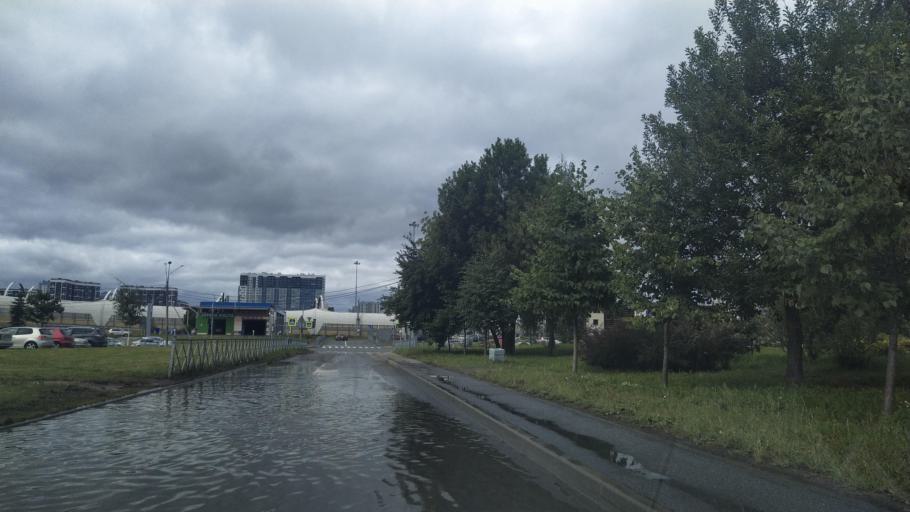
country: RU
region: St.-Petersburg
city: Staraya Derevnya
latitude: 59.9996
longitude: 30.2362
